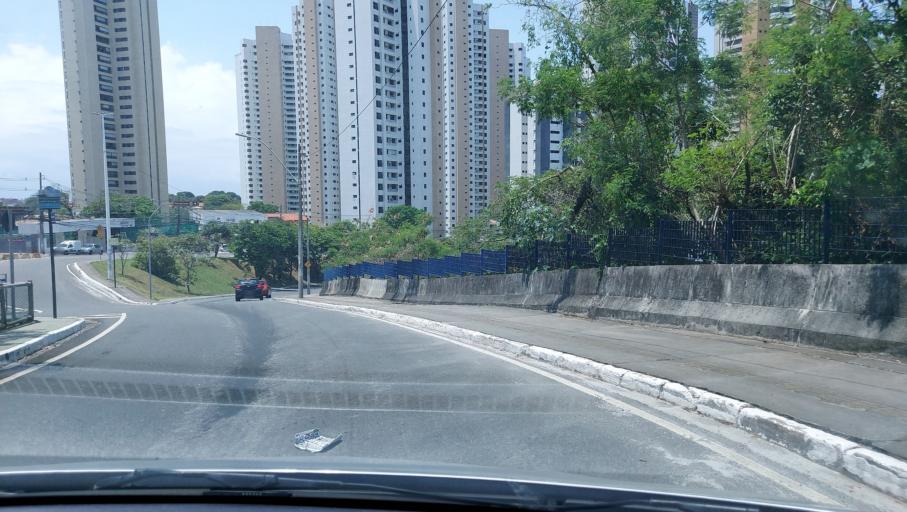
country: BR
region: Bahia
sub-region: Salvador
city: Salvador
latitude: -12.9979
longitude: -38.4889
